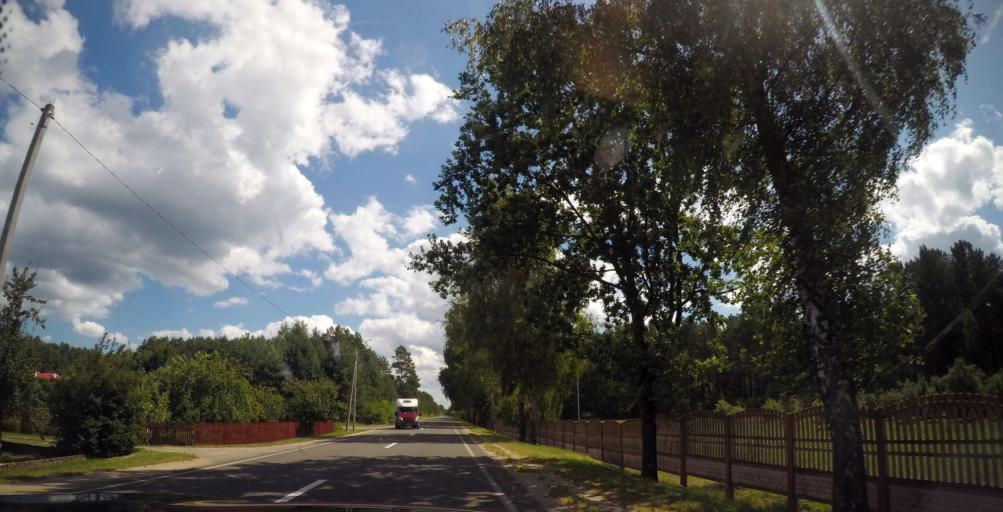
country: LT
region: Alytaus apskritis
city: Druskininkai
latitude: 53.8790
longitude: 24.1431
